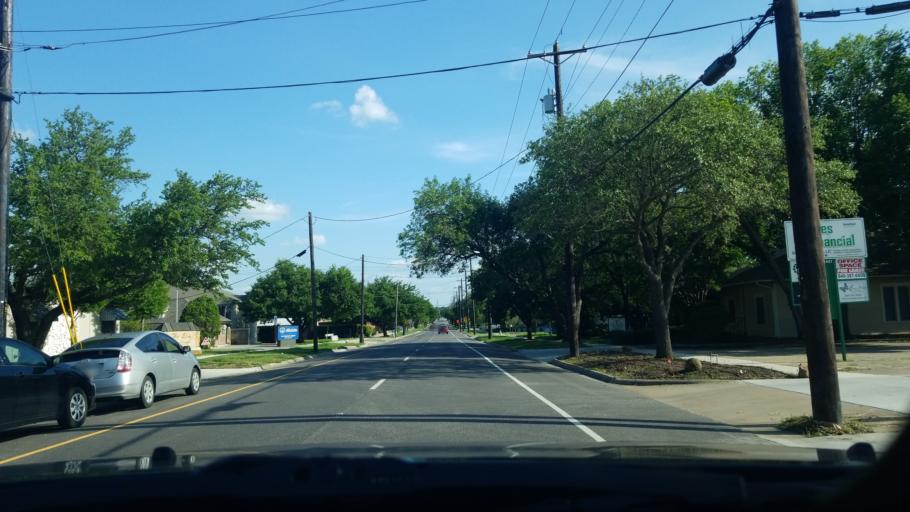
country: US
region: Texas
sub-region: Denton County
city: Denton
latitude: 33.2270
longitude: -97.1336
